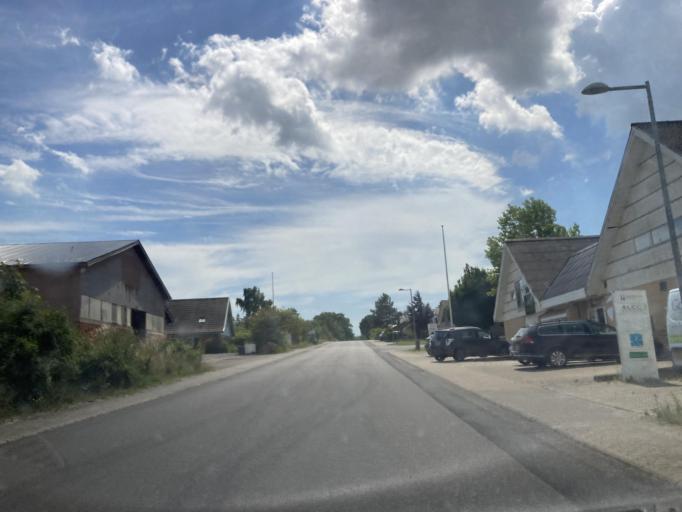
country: DK
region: Zealand
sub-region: Faxe Kommune
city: Haslev
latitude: 55.3250
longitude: 11.9370
